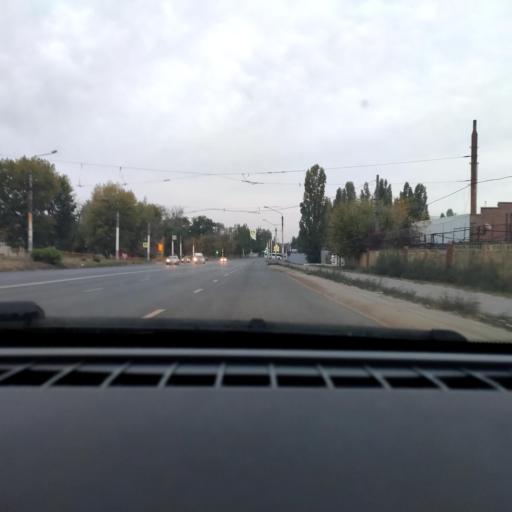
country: RU
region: Voronezj
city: Maslovka
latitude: 51.5996
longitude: 39.2481
